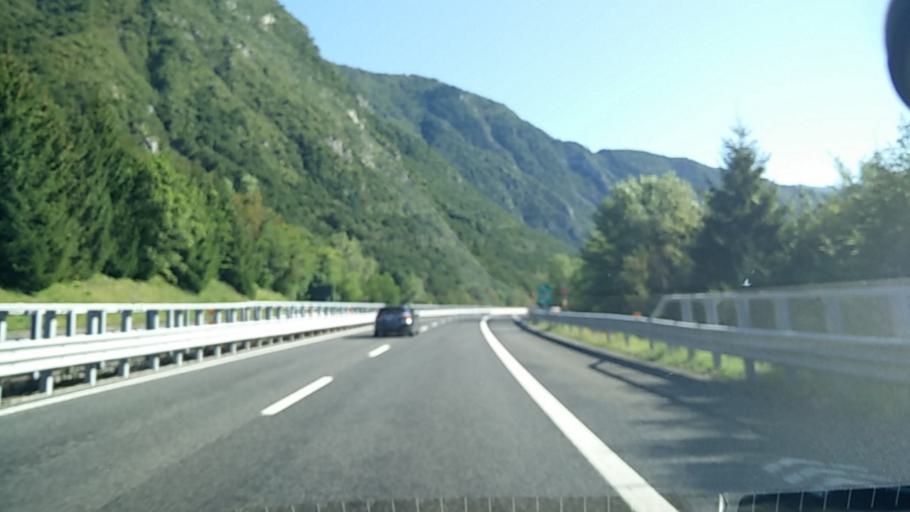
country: IT
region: Friuli Venezia Giulia
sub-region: Provincia di Udine
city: Amaro
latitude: 46.3822
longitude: 13.1195
